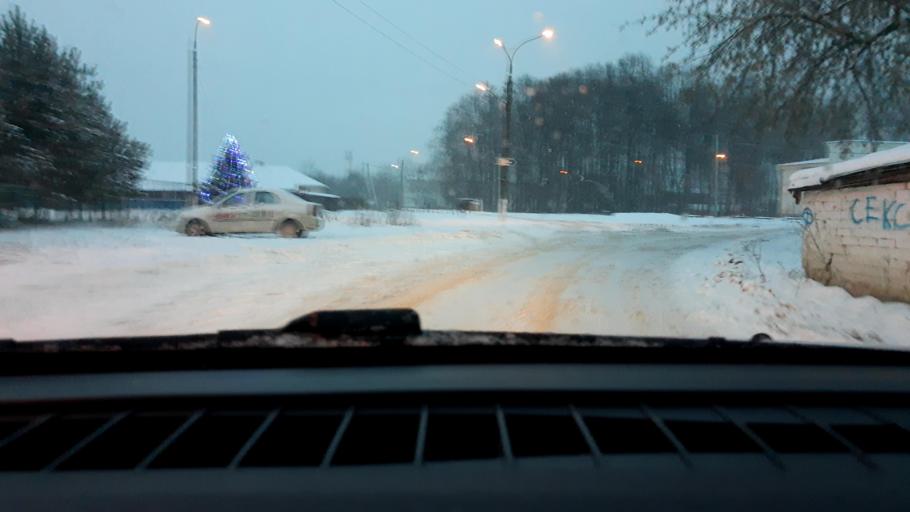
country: RU
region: Nizjnij Novgorod
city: Neklyudovo
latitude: 56.4029
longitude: 43.9903
